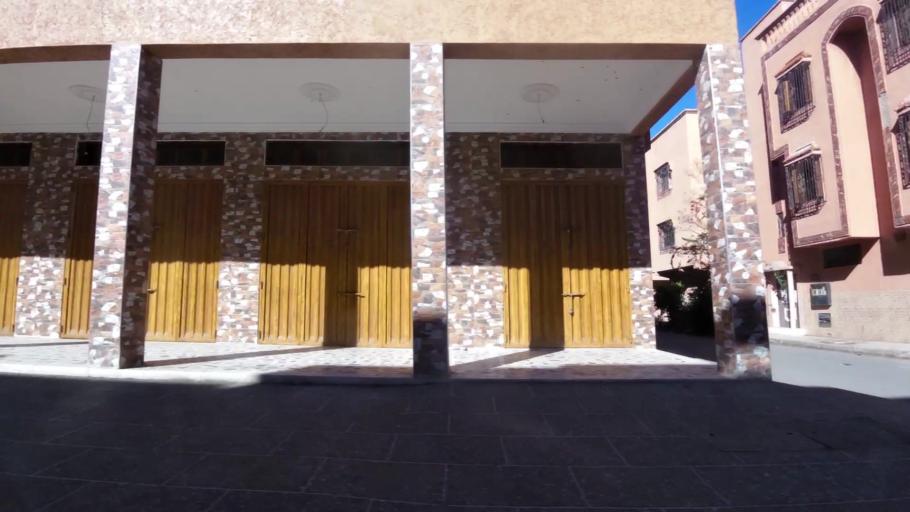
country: MA
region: Marrakech-Tensift-Al Haouz
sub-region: Marrakech
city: Marrakesh
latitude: 31.5977
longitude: -8.0418
